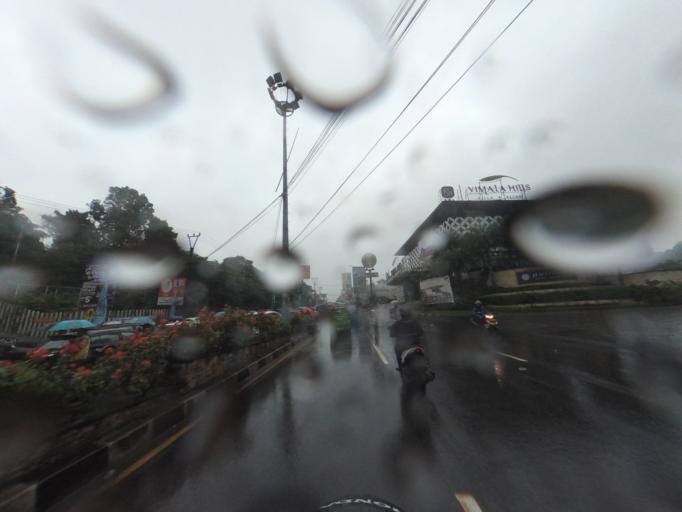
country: ID
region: West Java
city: Caringin
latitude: -6.6554
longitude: 106.8598
